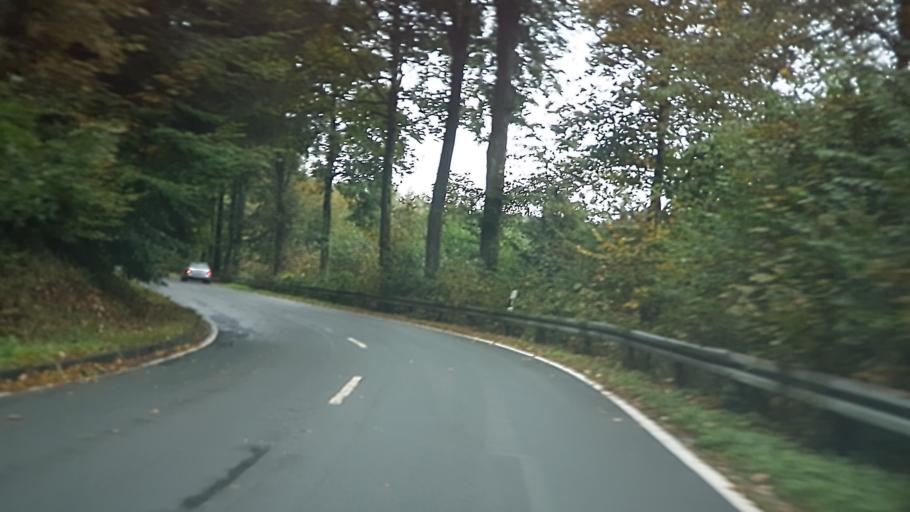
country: DE
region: North Rhine-Westphalia
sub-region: Regierungsbezirk Arnsberg
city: Luedenscheid
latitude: 51.1883
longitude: 7.6781
